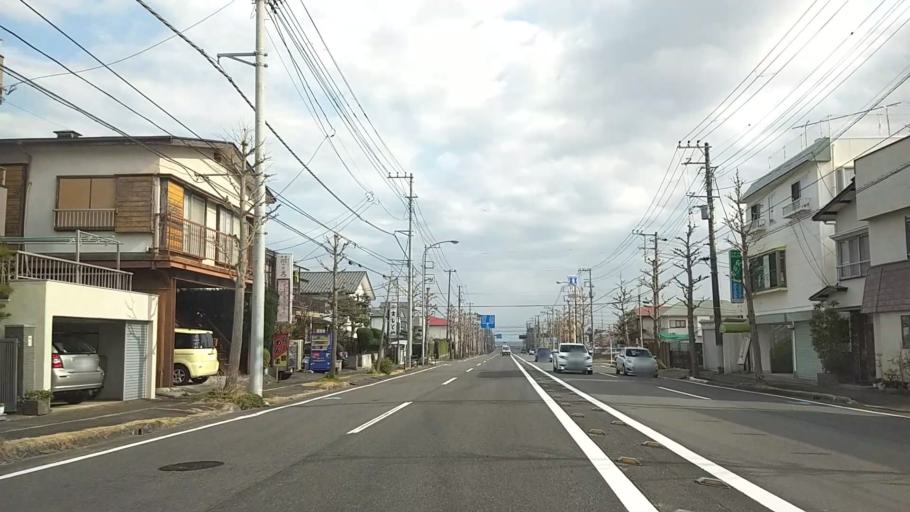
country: JP
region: Shizuoka
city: Ito
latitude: 35.0094
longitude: 139.0810
